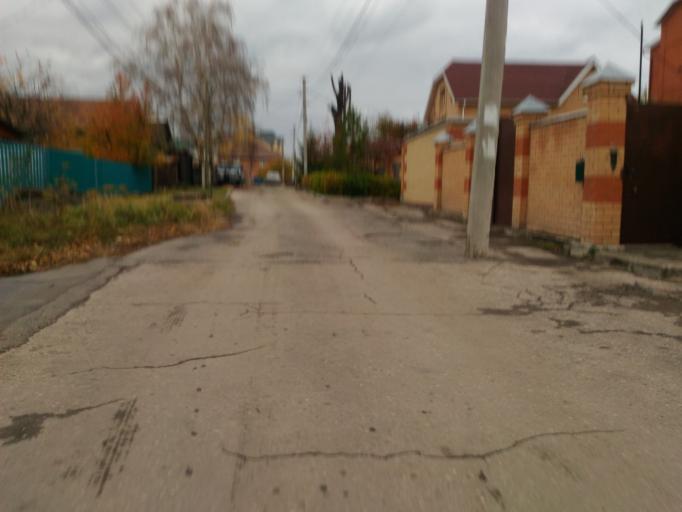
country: RU
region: Ulyanovsk
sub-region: Ulyanovskiy Rayon
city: Ulyanovsk
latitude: 54.3363
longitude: 48.3912
